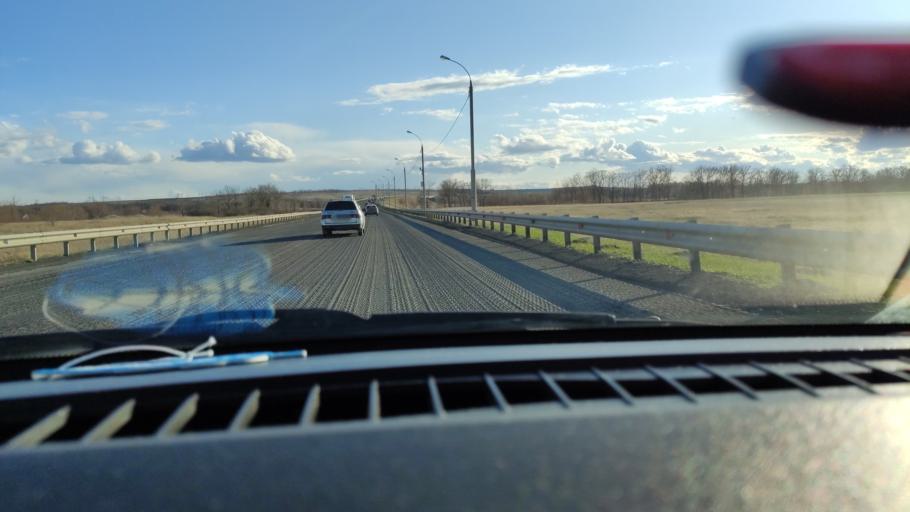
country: RU
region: Saratov
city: Yelshanka
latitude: 51.8030
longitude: 46.1908
